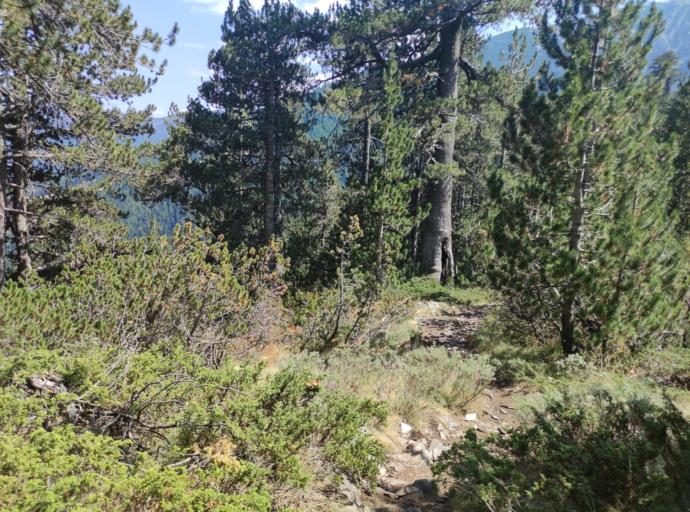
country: BG
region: Blagoevgrad
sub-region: Obshtina Bansko
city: Bansko
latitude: 41.7726
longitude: 23.4230
